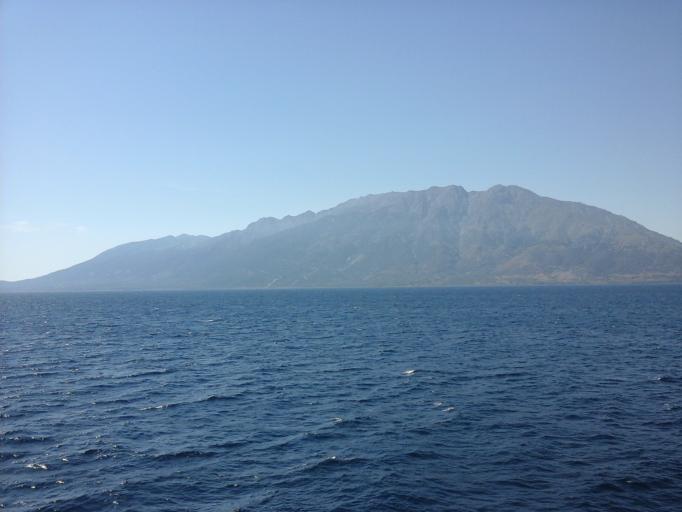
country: GR
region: East Macedonia and Thrace
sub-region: Nomos Evrou
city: Samothraki
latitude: 40.5635
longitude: 25.5602
